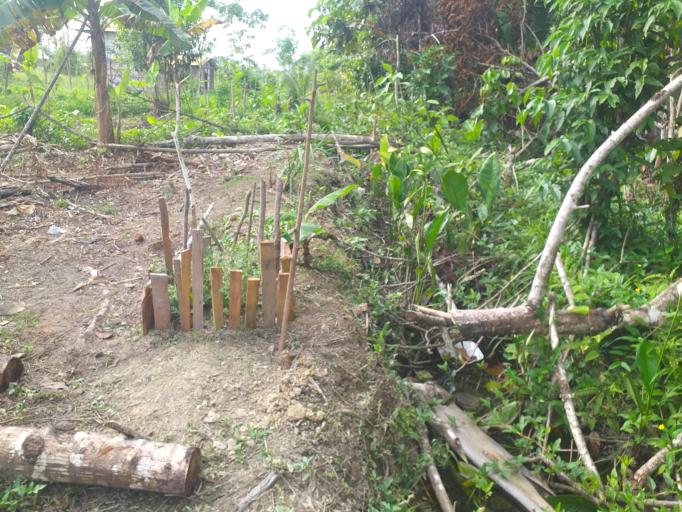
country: CO
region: Narino
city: La Tola
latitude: 2.3399
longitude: -78.3243
